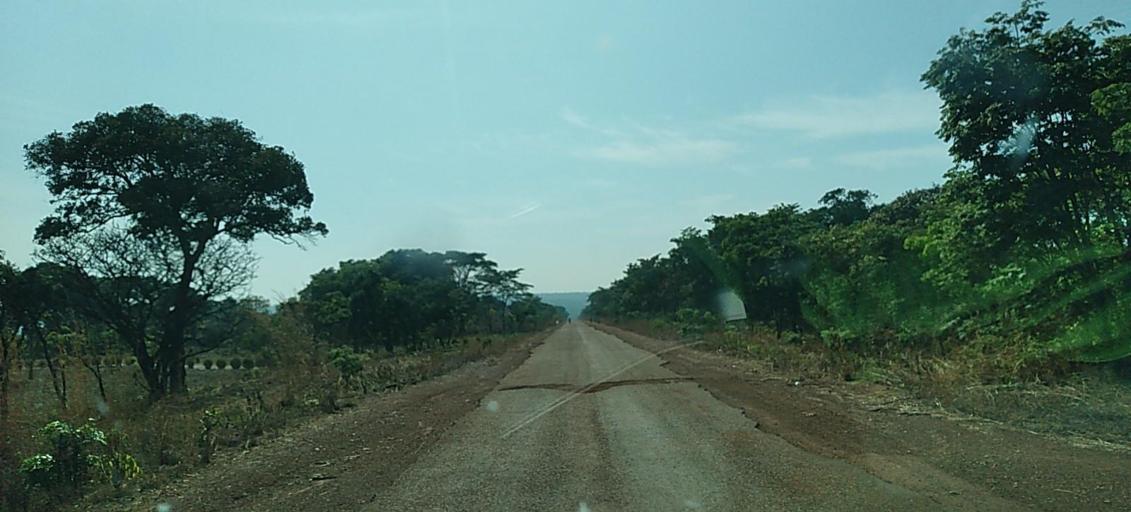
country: ZM
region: North-Western
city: Mwinilunga
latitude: -11.8221
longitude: 25.1053
